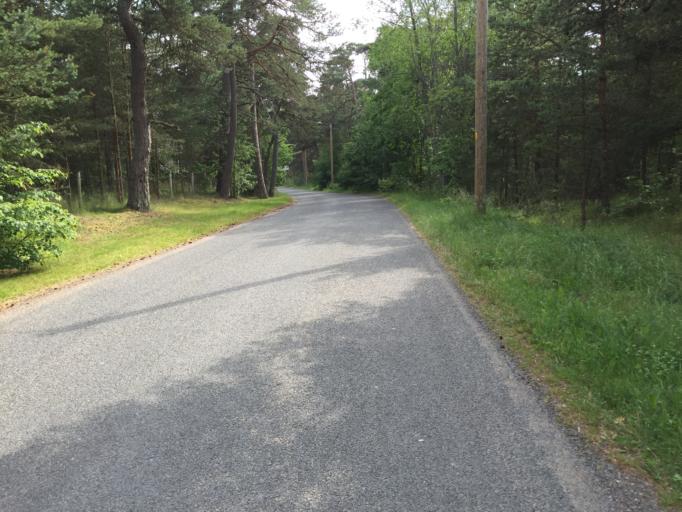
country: EE
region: Harju
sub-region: Raasiku vald
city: Raasiku
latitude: 59.5142
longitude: 25.2710
